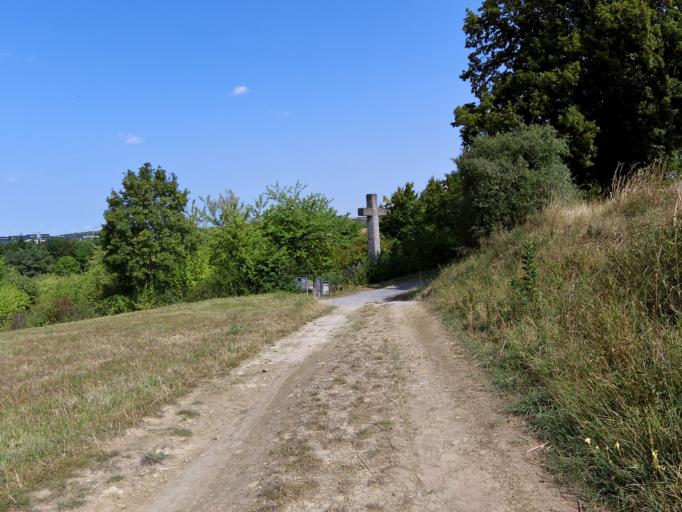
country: DE
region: Bavaria
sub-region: Regierungsbezirk Unterfranken
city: Estenfeld
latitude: 49.8317
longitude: 10.0142
